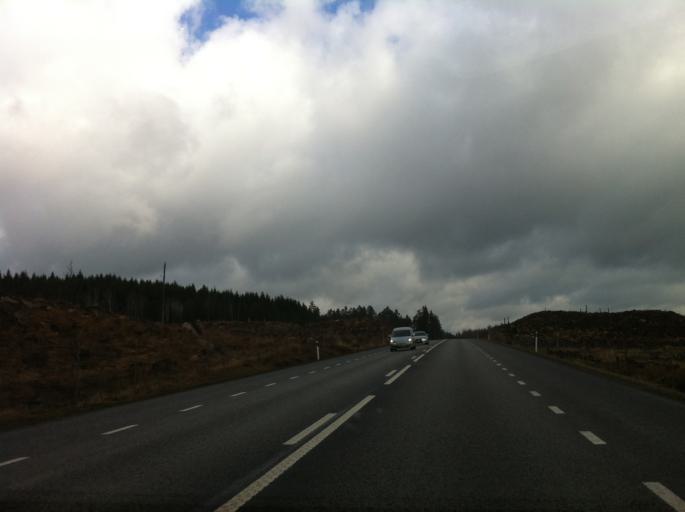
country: SE
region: Halland
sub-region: Halmstads Kommun
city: Aled
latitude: 56.7730
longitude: 12.9508
